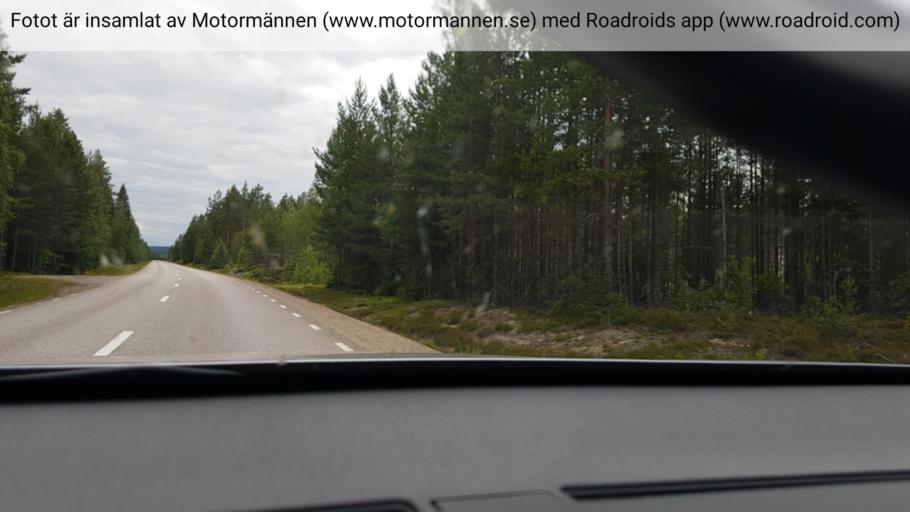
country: NO
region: Hedmark
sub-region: Trysil
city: Innbygda
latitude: 60.9294
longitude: 12.5064
